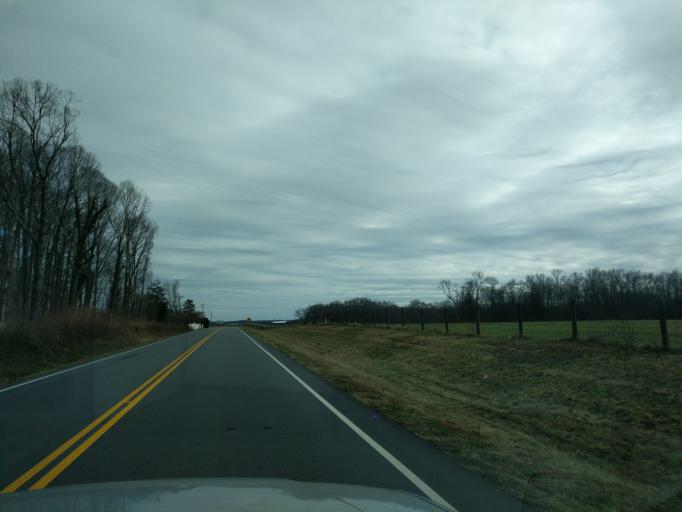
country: US
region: South Carolina
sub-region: Oconee County
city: Utica
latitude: 34.5878
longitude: -82.9506
